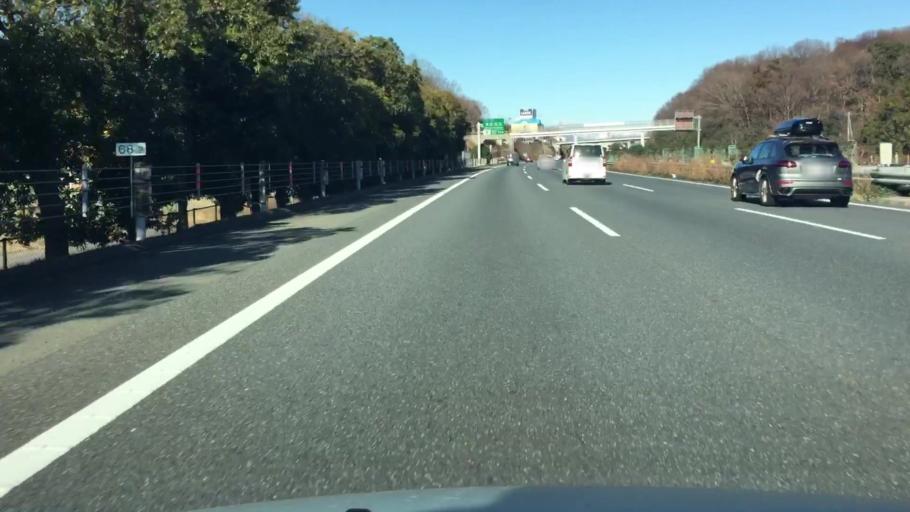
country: JP
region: Saitama
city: Honjo
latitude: 36.2075
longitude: 139.1722
